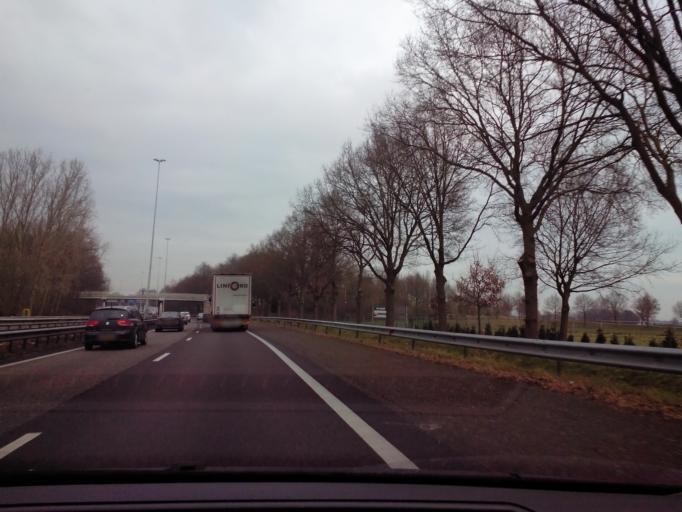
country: NL
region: North Brabant
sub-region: Gemeente Oosterhout
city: Oosterhout
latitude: 51.6371
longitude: 4.8823
